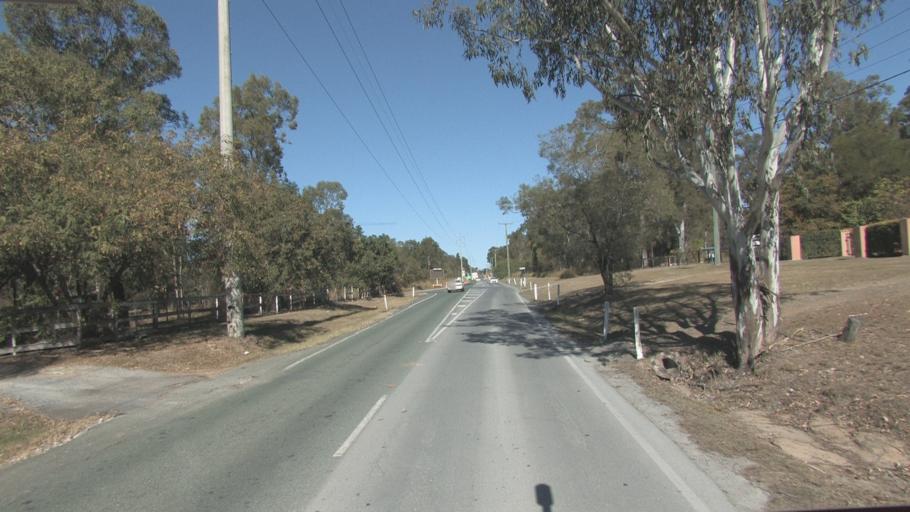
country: AU
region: Queensland
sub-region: Logan
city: Cedar Vale
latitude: -27.8505
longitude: 153.0210
